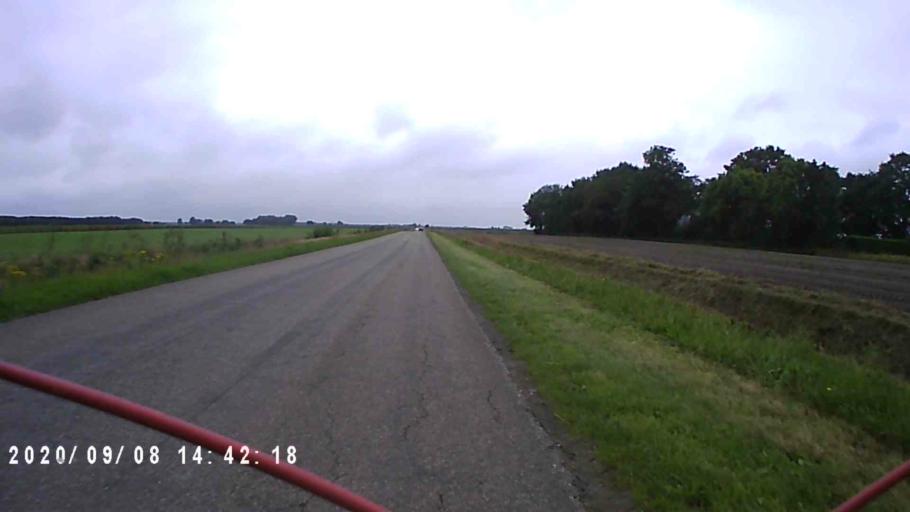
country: NL
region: Groningen
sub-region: Gemeente Slochteren
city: Slochteren
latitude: 53.2392
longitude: 6.8261
